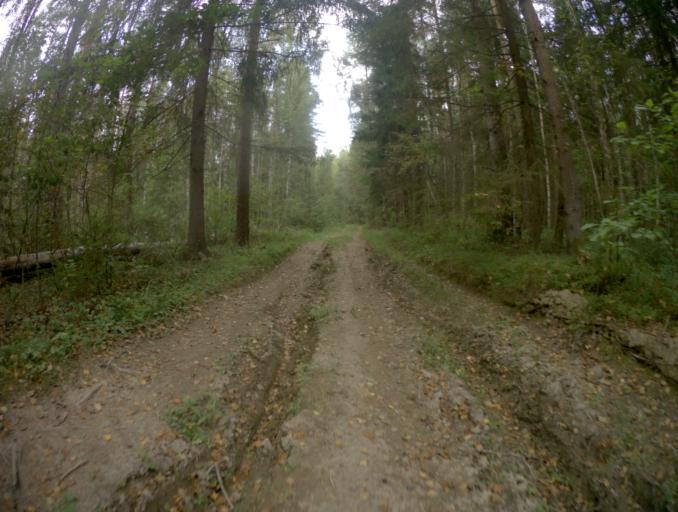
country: RU
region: Vladimir
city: Golovino
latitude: 55.9181
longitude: 40.5002
